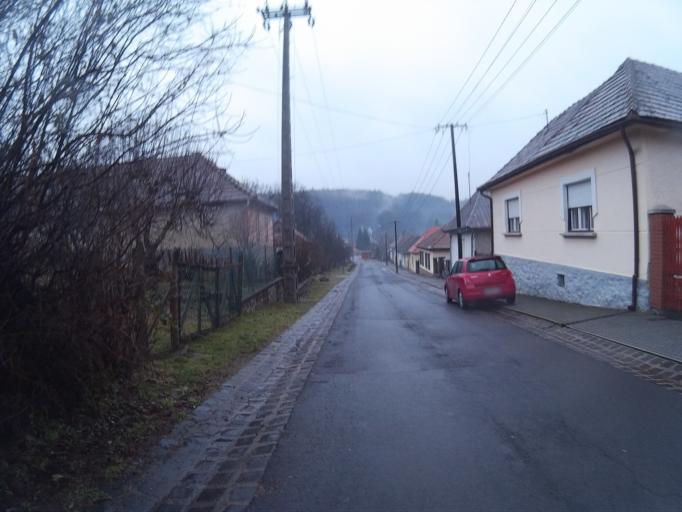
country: HU
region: Nograd
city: Somoskoujfalu
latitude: 48.1690
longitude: 19.8571
